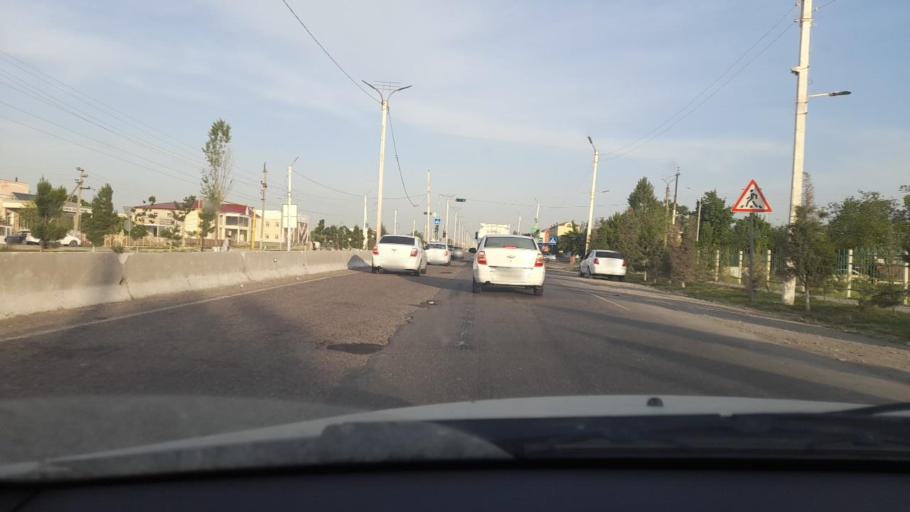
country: KZ
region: Ongtustik Qazaqstan
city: Myrzakent
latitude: 40.5481
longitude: 68.4063
